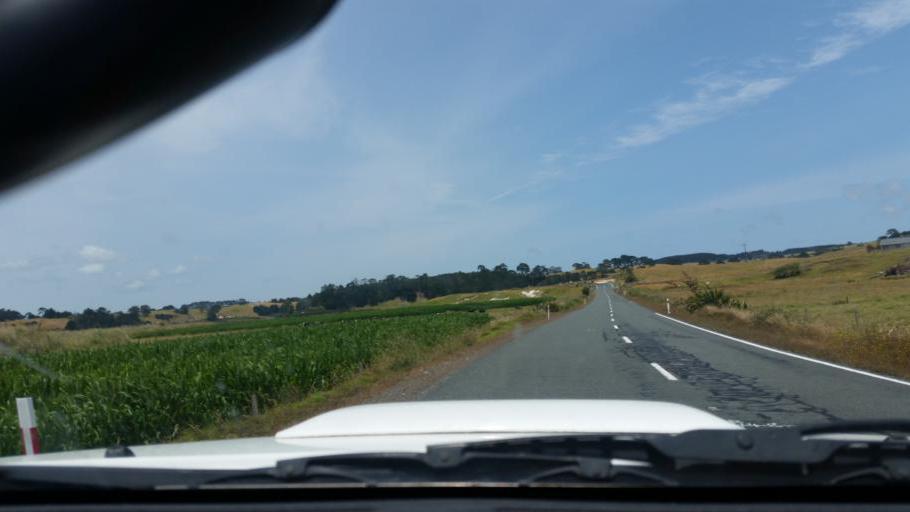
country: NZ
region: Northland
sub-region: Kaipara District
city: Dargaville
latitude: -36.1842
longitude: 174.0325
